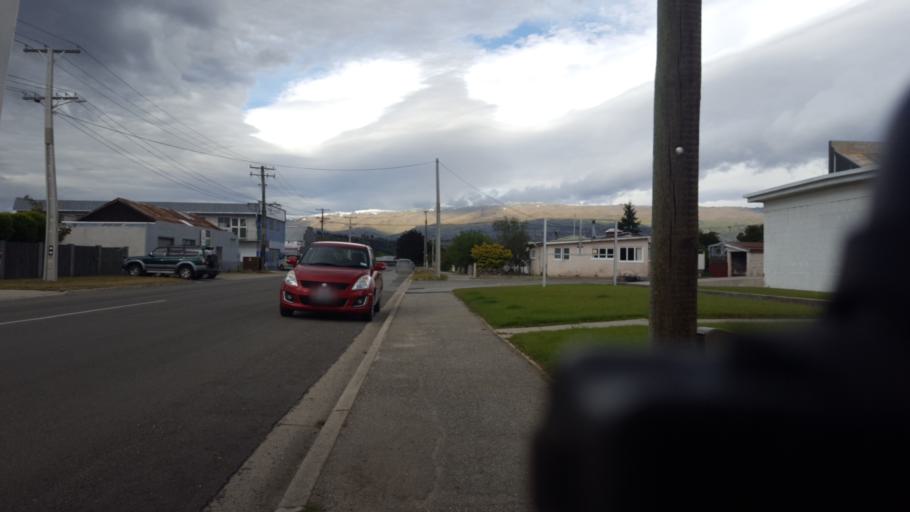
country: NZ
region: Otago
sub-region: Queenstown-Lakes District
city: Wanaka
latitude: -45.2466
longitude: 169.3939
